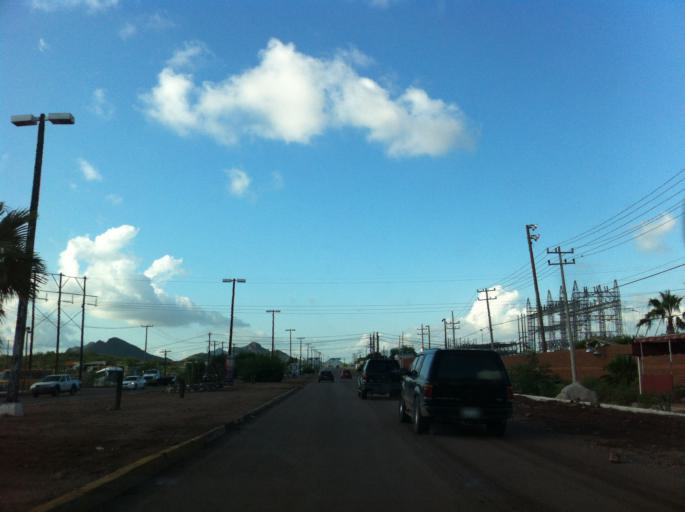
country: MX
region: Sonora
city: Heroica Guaymas
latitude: 27.9457
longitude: -110.9330
